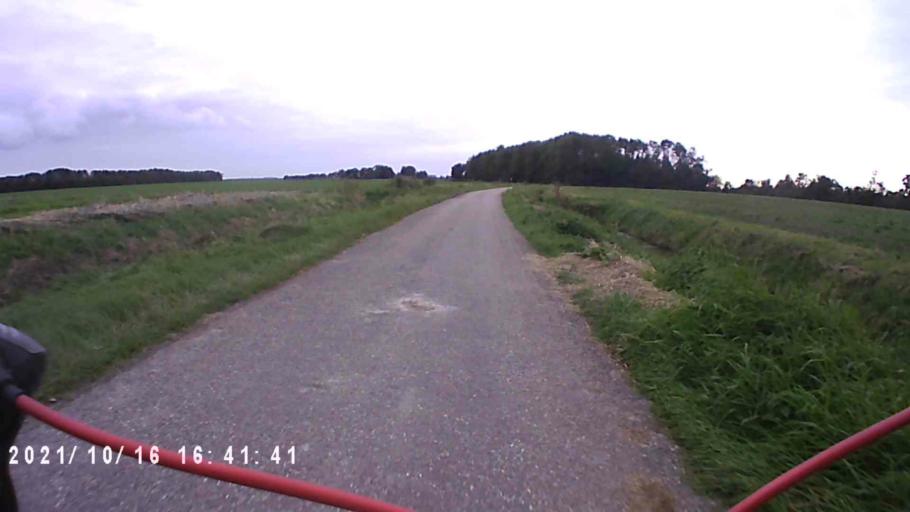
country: NL
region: Friesland
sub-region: Gemeente Dongeradeel
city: Anjum
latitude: 53.3764
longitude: 6.1439
